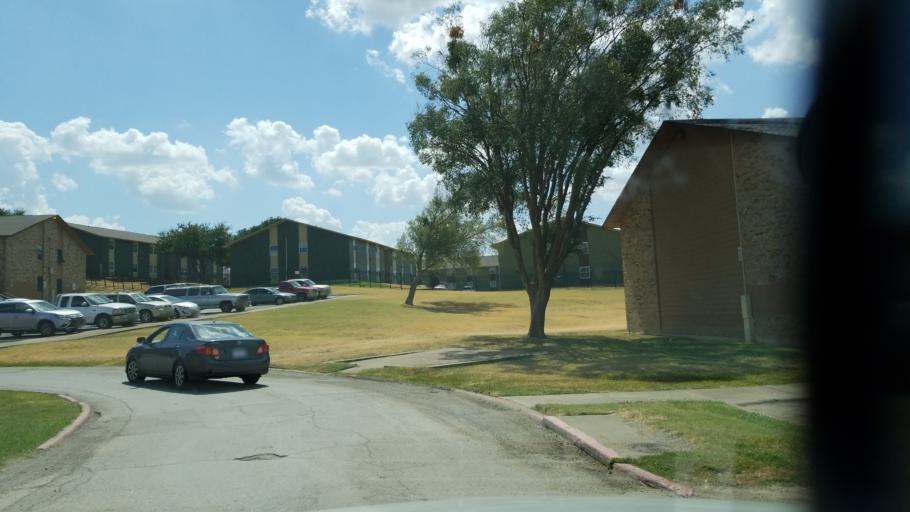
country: US
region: Texas
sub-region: Dallas County
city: Cockrell Hill
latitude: 32.7415
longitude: -96.9142
